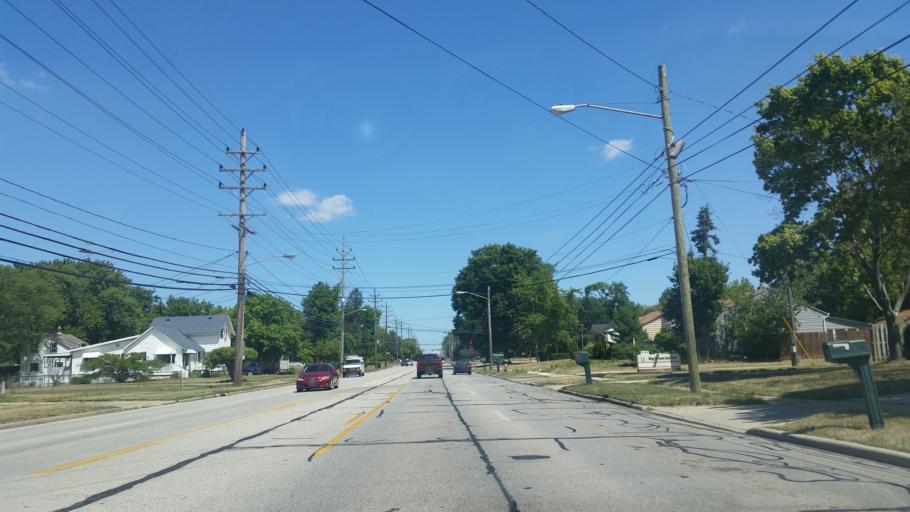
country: US
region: Ohio
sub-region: Cuyahoga County
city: Brook Park
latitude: 41.3965
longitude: -81.7843
